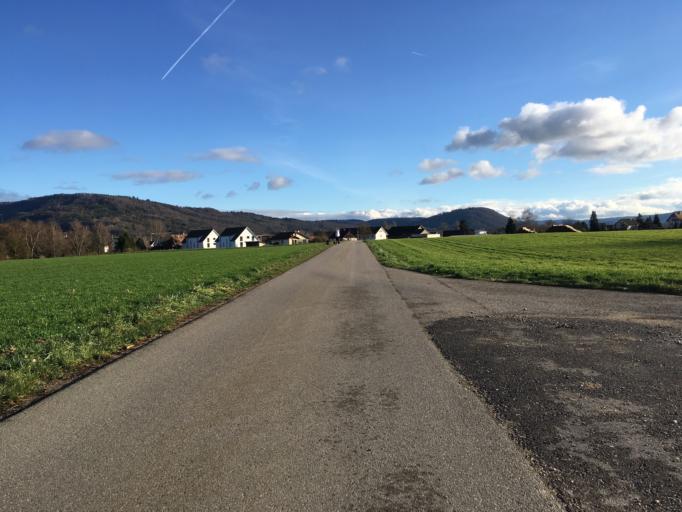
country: CH
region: Schaffhausen
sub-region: Bezirk Stein
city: Ramsen
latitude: 47.7084
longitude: 8.8022
